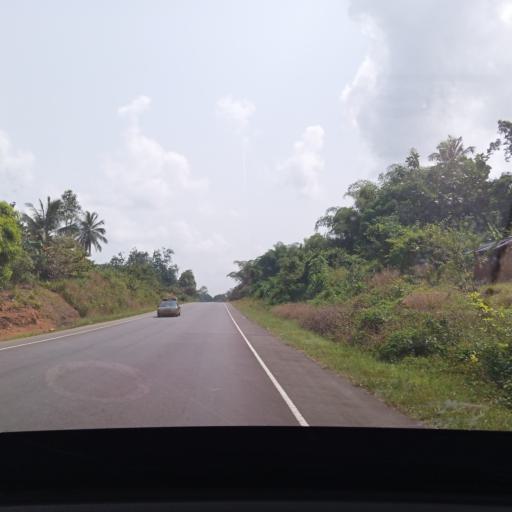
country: LR
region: Margibi
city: Kakata
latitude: 6.2520
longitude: -10.3008
